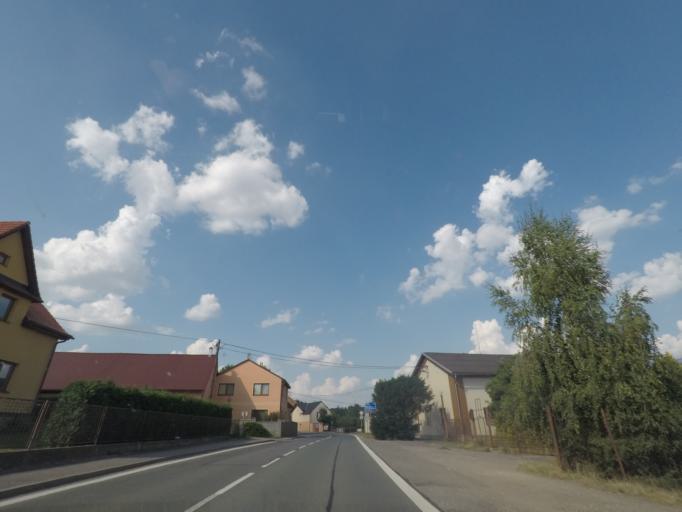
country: CZ
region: Kralovehradecky
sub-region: Okres Nachod
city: Jaromer
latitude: 50.3785
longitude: 15.9175
